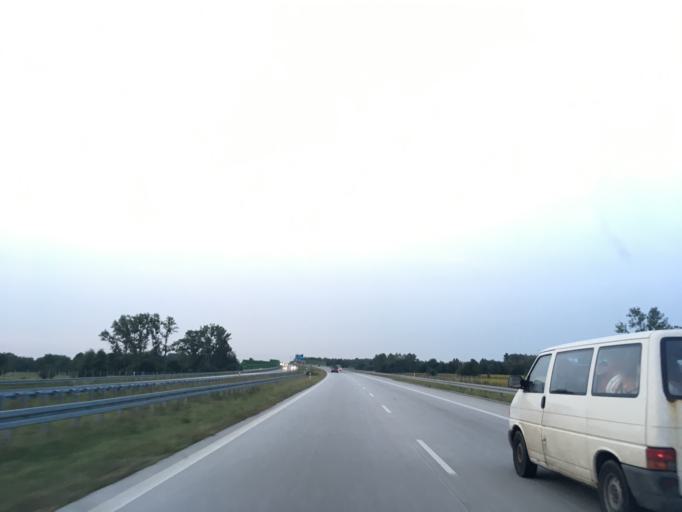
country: PL
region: Lodz Voivodeship
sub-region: Powiat lodzki wschodni
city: Andrespol
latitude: 51.7616
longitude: 19.5957
